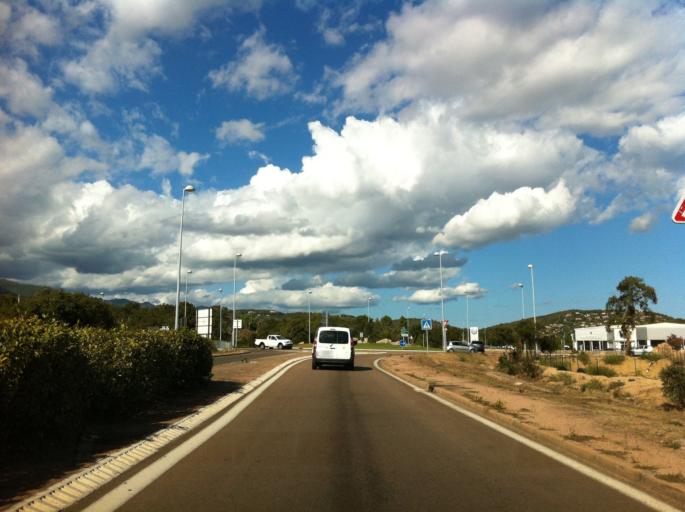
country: FR
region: Corsica
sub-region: Departement de la Corse-du-Sud
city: Porto-Vecchio
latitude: 41.6011
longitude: 9.2685
